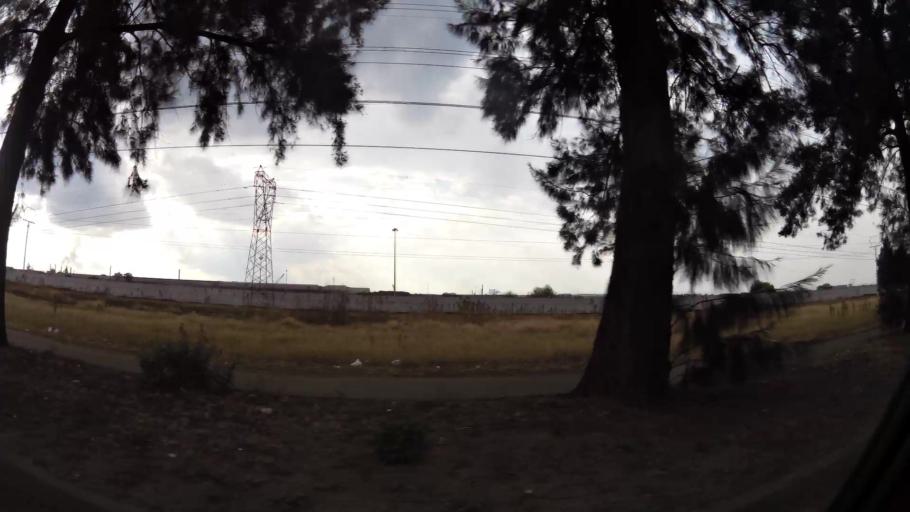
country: ZA
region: Gauteng
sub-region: Sedibeng District Municipality
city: Vanderbijlpark
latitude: -26.6739
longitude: 27.8297
